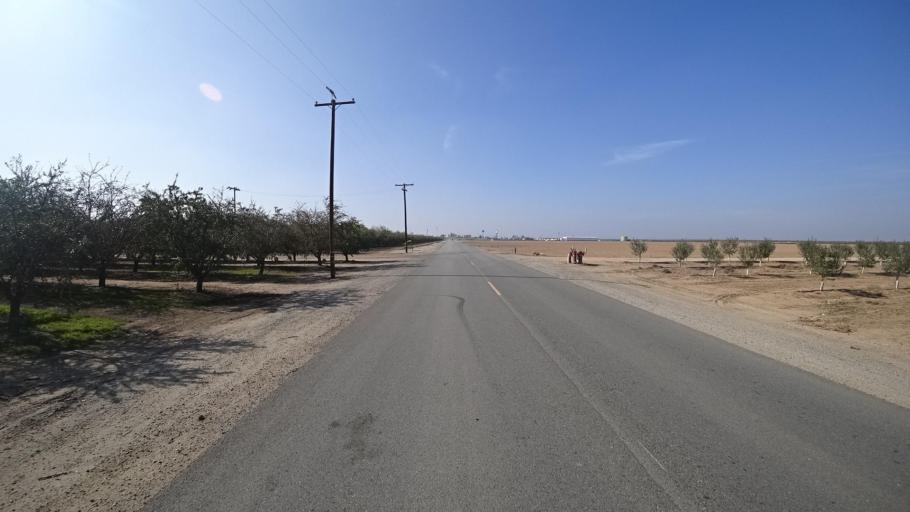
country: US
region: California
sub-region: Kern County
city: Shafter
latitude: 35.5294
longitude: -119.1782
